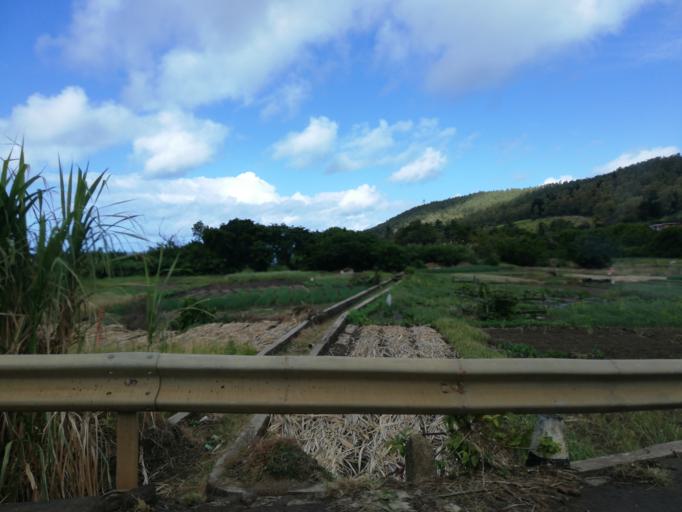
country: MU
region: Grand Port
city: Bambous Virieux
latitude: -20.3315
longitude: 57.7673
